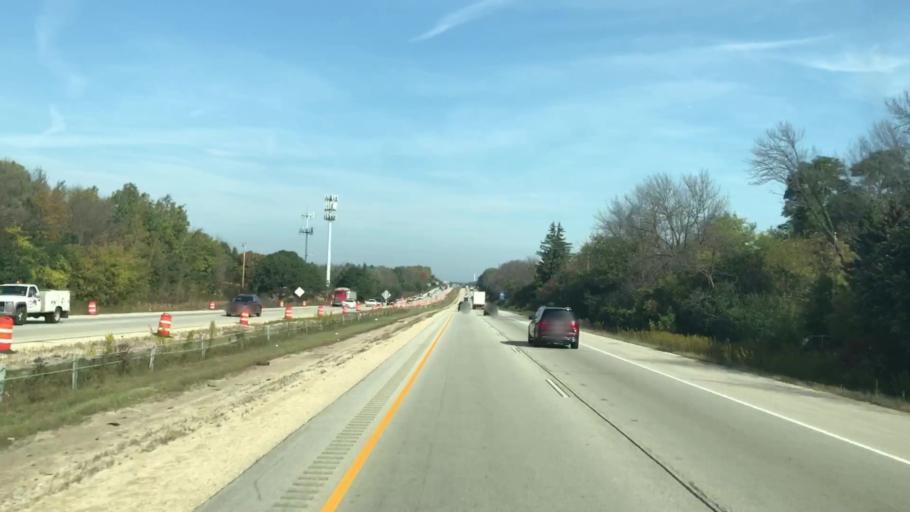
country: US
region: Wisconsin
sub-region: Milwaukee County
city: Fox Point
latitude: 43.1536
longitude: -87.9160
